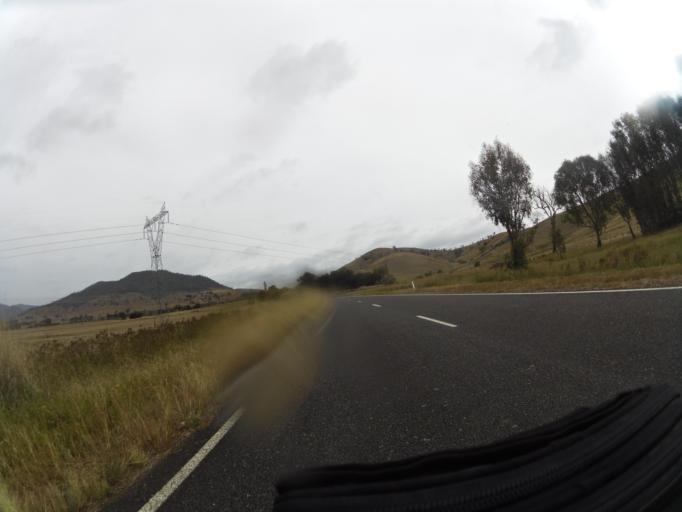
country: AU
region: New South Wales
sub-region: Greater Hume Shire
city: Holbrook
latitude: -36.2089
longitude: 147.7344
